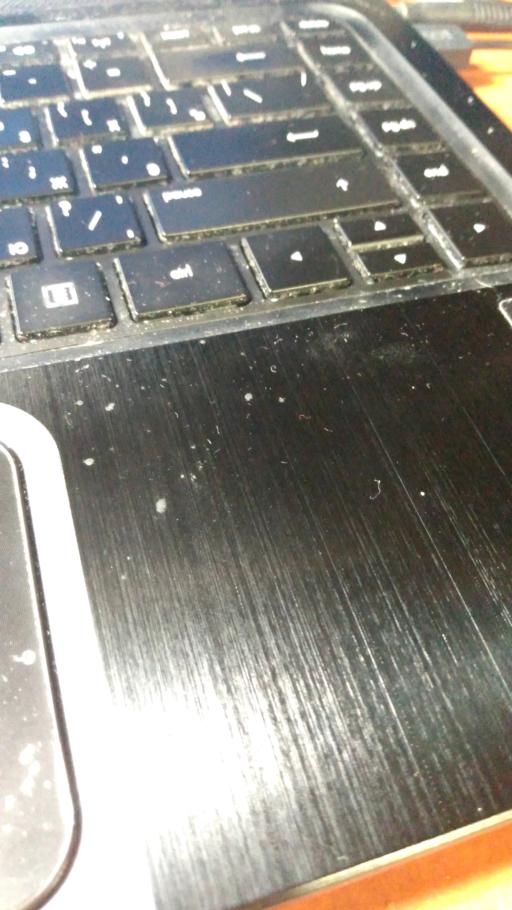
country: RU
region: Tverskaya
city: Vyshniy Volochek
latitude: 57.6667
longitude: 34.6767
